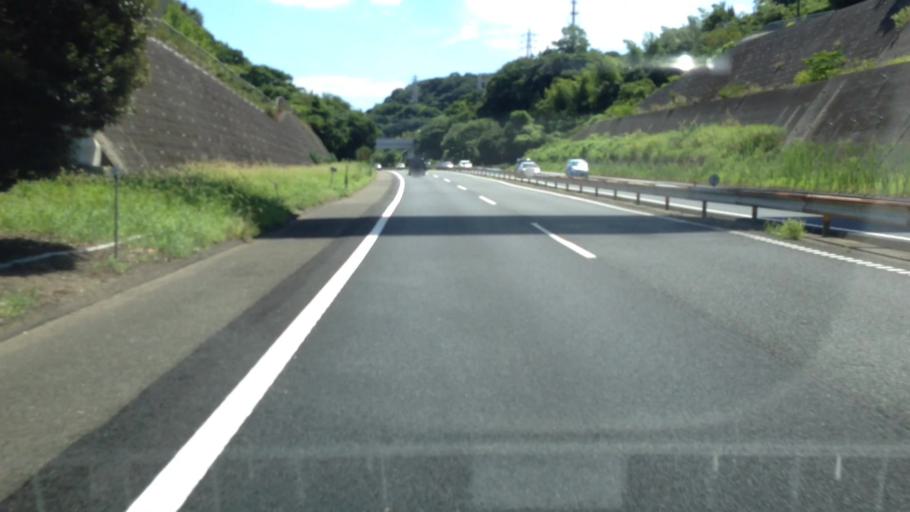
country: JP
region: Kanagawa
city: Yokosuka
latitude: 35.2617
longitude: 139.6330
